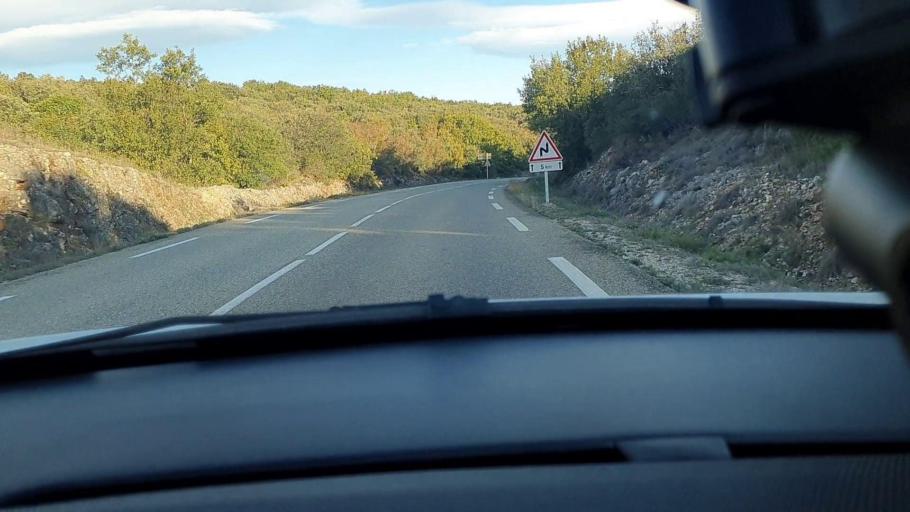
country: FR
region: Languedoc-Roussillon
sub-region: Departement du Gard
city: Barjac
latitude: 44.2220
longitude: 4.3203
